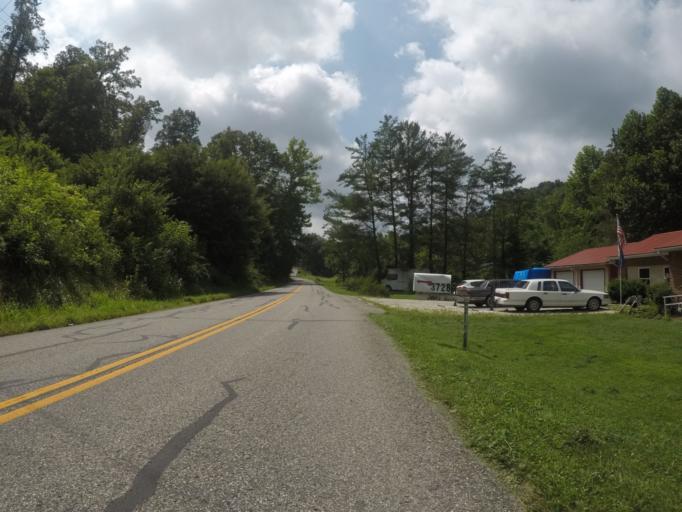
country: US
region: Kentucky
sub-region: Boyd County
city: Meads
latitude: 38.4050
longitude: -82.6599
